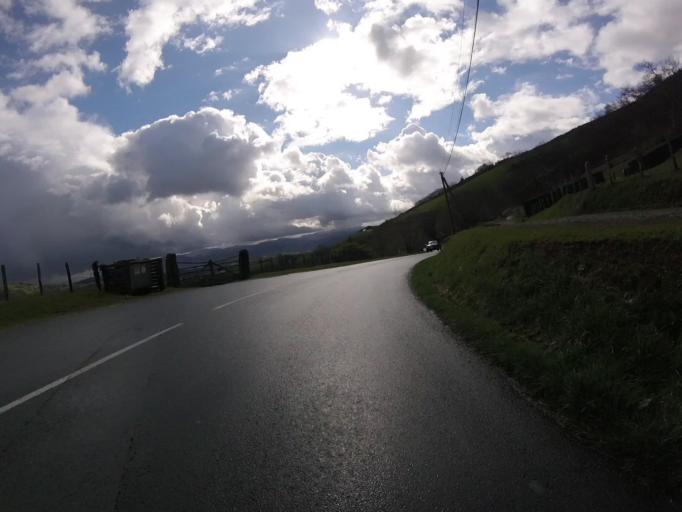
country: FR
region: Aquitaine
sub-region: Departement des Pyrenees-Atlantiques
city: Sare
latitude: 43.3187
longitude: -1.5980
